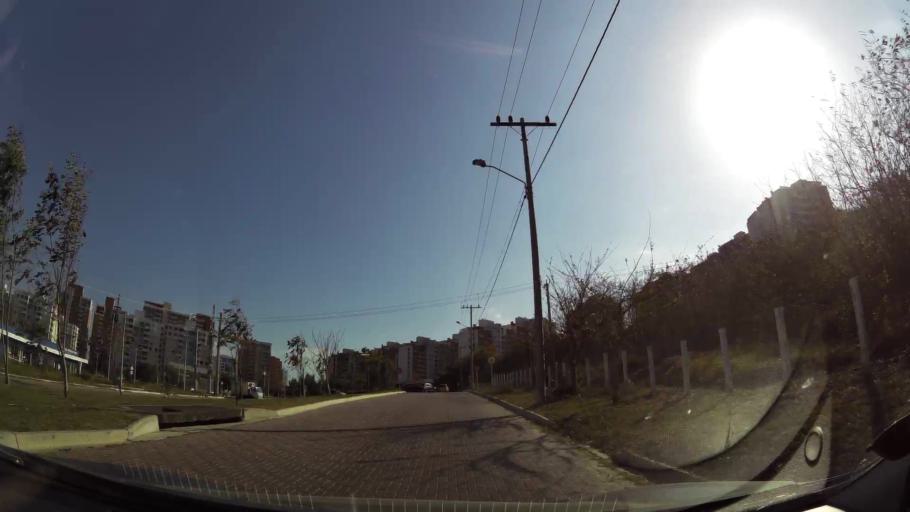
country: CO
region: Atlantico
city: Barranquilla
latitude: 11.0058
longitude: -74.8359
